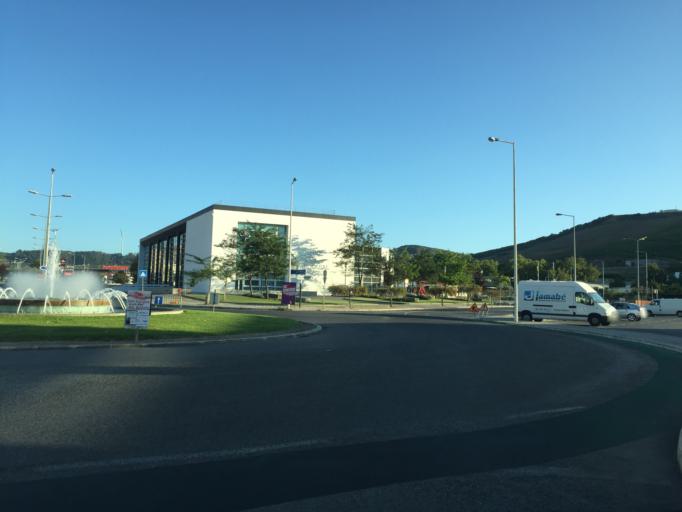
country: PT
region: Lisbon
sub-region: Torres Vedras
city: Torres Vedras
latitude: 39.0844
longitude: -9.2612
